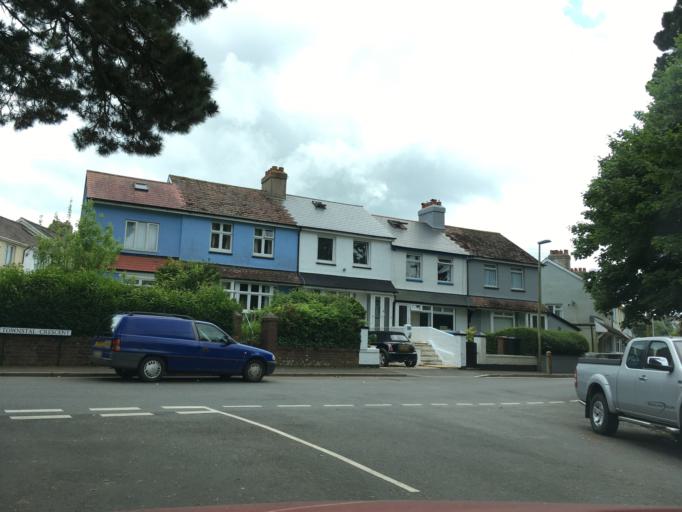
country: GB
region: England
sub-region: Devon
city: Dartmouth
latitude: 50.3533
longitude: -3.5919
